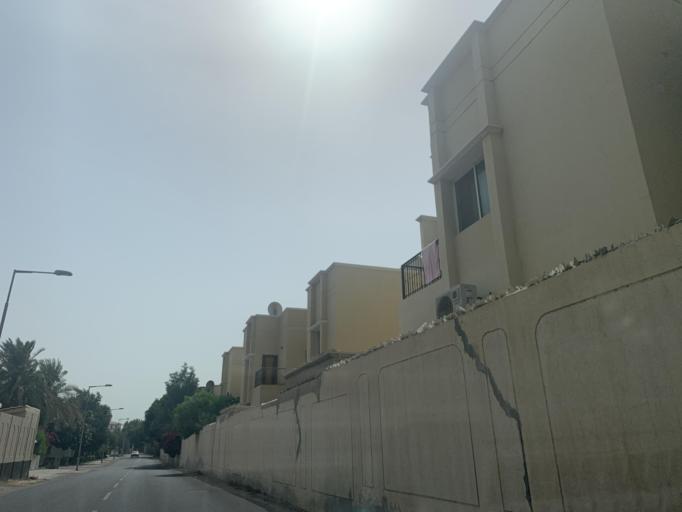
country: BH
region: Manama
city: Jidd Hafs
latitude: 26.2035
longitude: 50.4796
